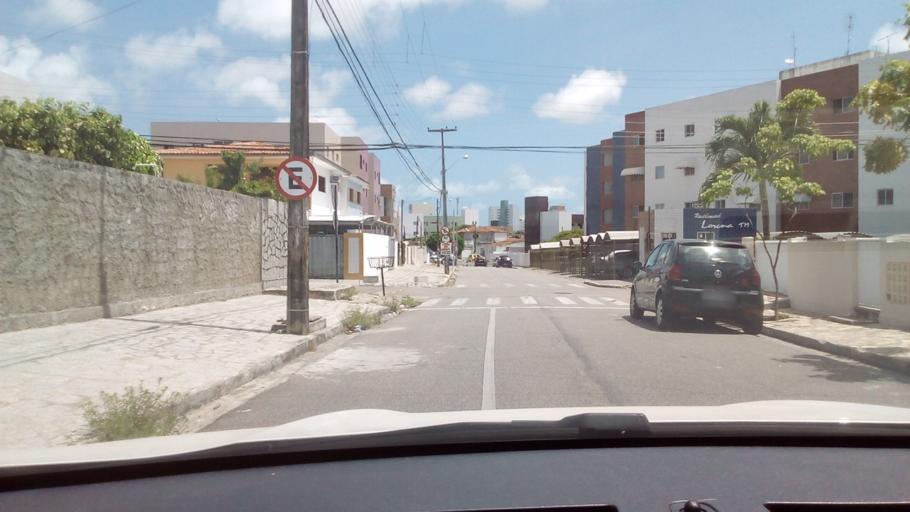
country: BR
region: Paraiba
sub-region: Joao Pessoa
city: Joao Pessoa
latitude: -7.1491
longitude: -34.8452
